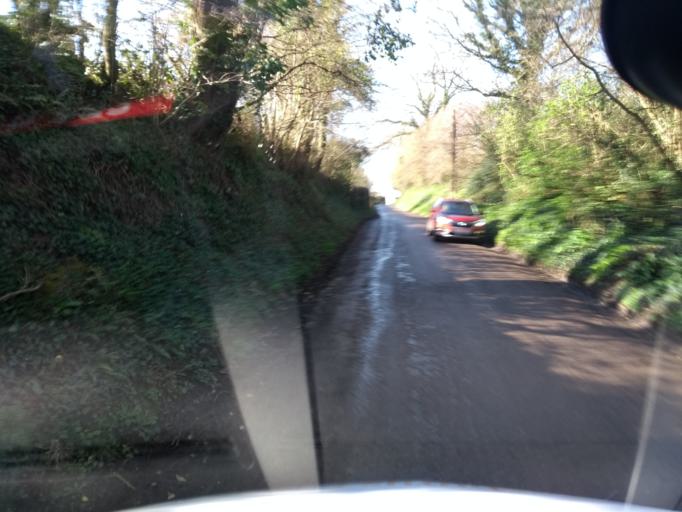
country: GB
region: England
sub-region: Somerset
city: South Petherton
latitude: 50.9773
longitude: -2.8324
